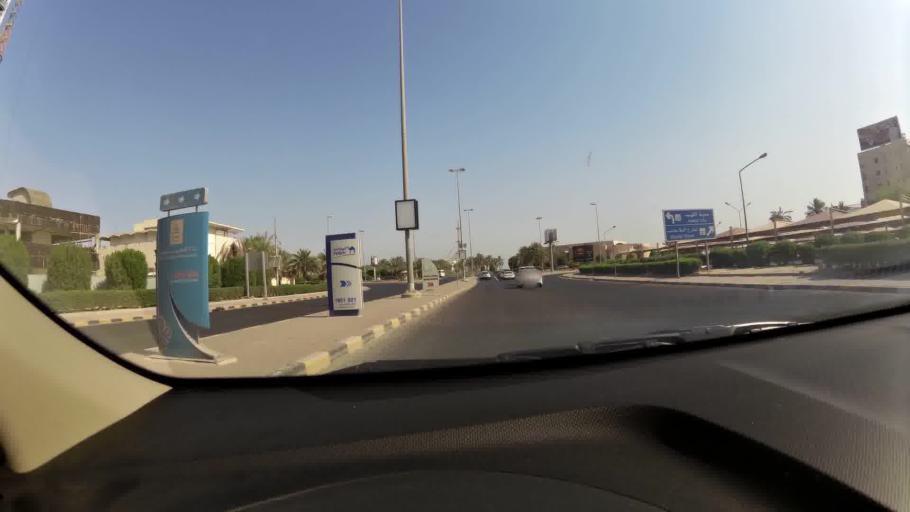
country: KW
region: Muhafazat Hawalli
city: As Salimiyah
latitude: 29.3408
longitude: 48.0696
